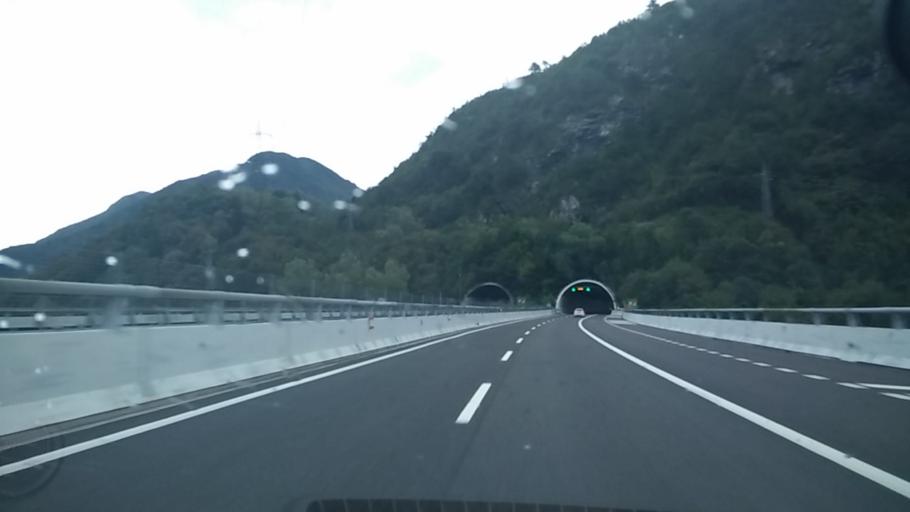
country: IT
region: Friuli Venezia Giulia
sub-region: Provincia di Udine
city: Amaro
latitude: 46.3392
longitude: 13.0717
